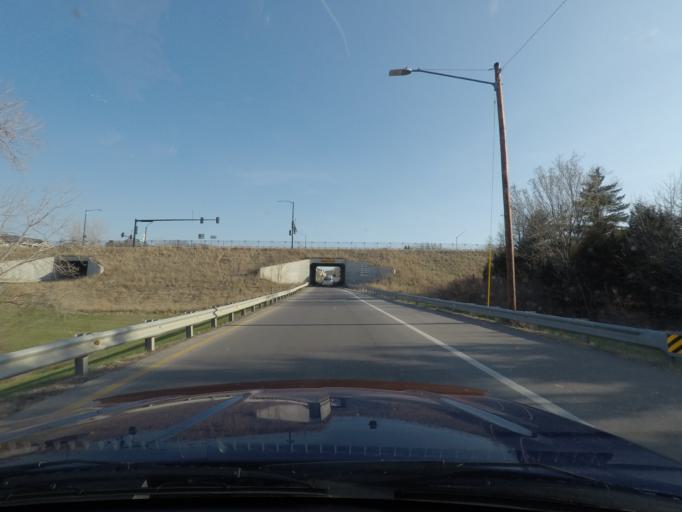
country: US
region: Kansas
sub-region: Douglas County
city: Lawrence
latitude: 38.9735
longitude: -95.2612
